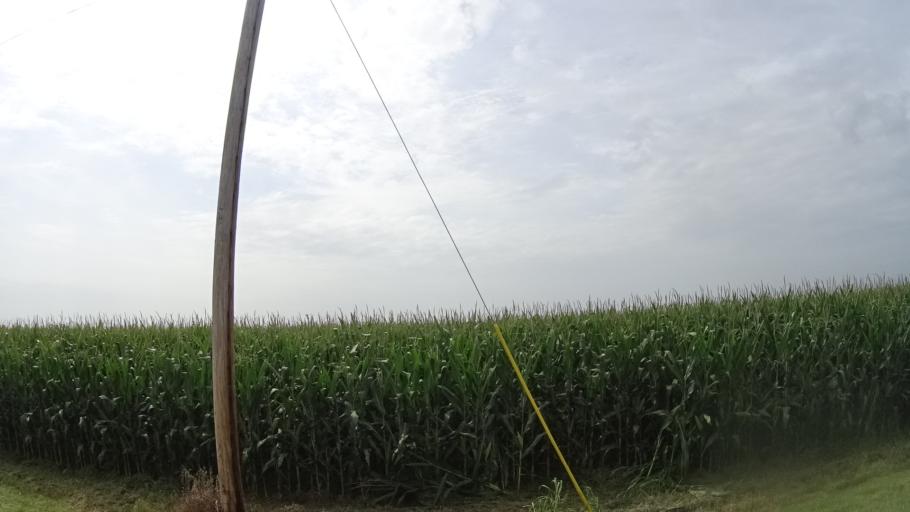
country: US
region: Indiana
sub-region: Madison County
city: Ingalls
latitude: 40.0066
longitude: -85.8130
